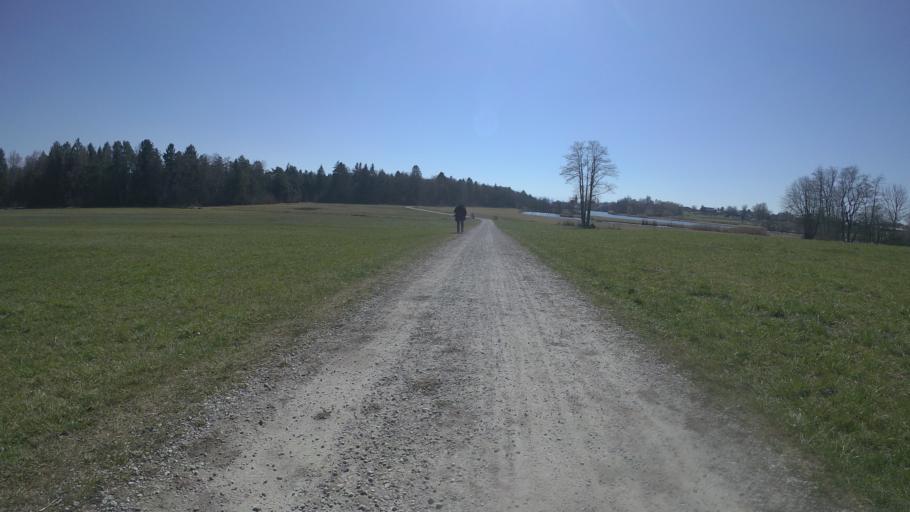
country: DE
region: Bavaria
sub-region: Upper Bavaria
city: Seeon-Seebruck
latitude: 47.9405
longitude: 12.4943
